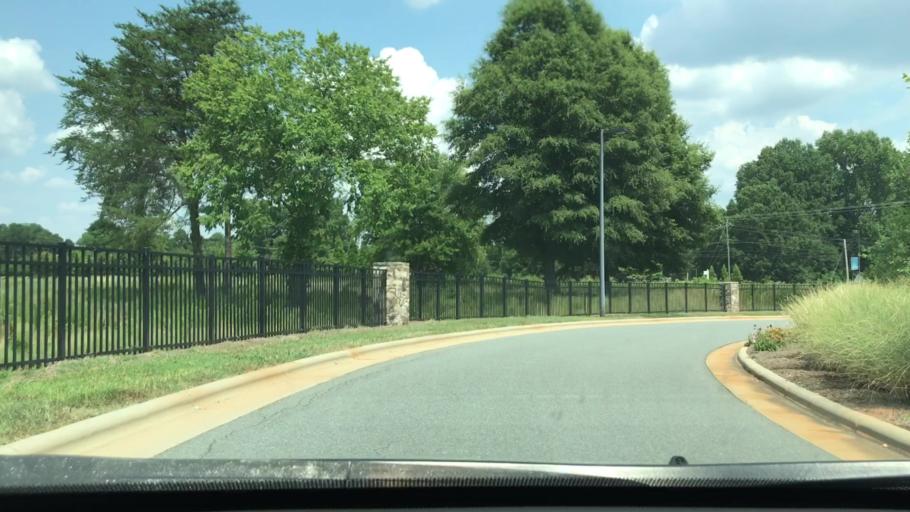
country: US
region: North Carolina
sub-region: Gaston County
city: Davidson
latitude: 35.5357
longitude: -80.8542
